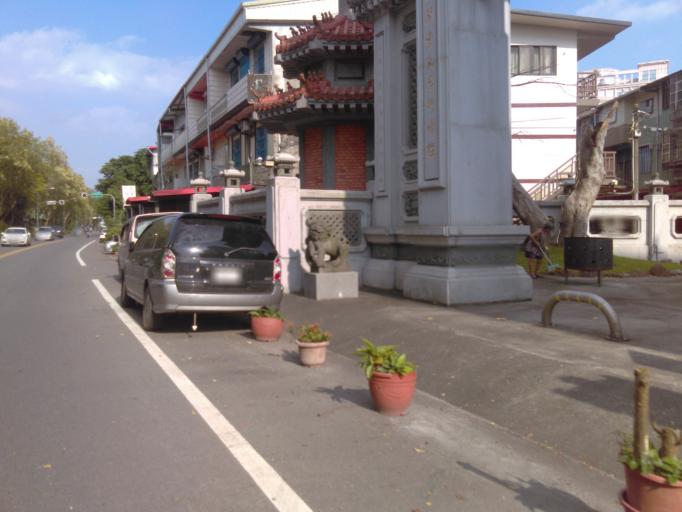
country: TW
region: Taiwan
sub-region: Yilan
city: Yilan
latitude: 24.7629
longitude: 121.7514
